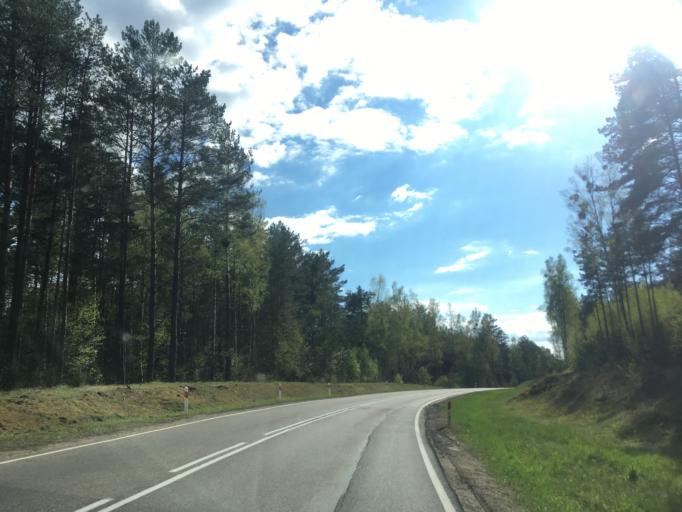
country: PL
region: Warmian-Masurian Voivodeship
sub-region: Powiat szczycienski
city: Jedwabno
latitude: 53.5415
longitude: 20.8360
